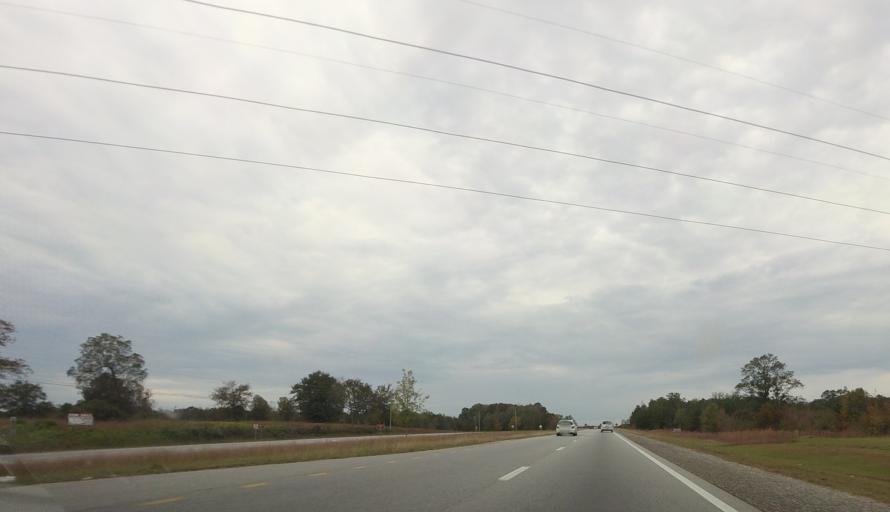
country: US
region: Alabama
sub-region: Lee County
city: Opelika
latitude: 32.6269
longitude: -85.2802
